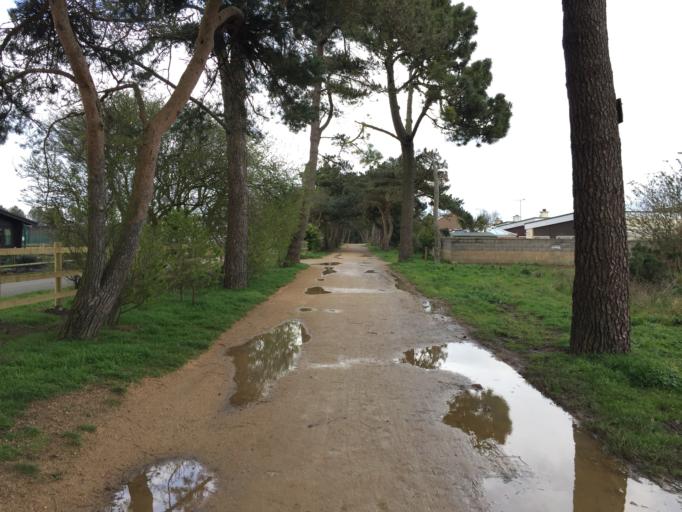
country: JE
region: St Helier
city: Saint Helier
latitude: 49.1932
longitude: -2.2055
